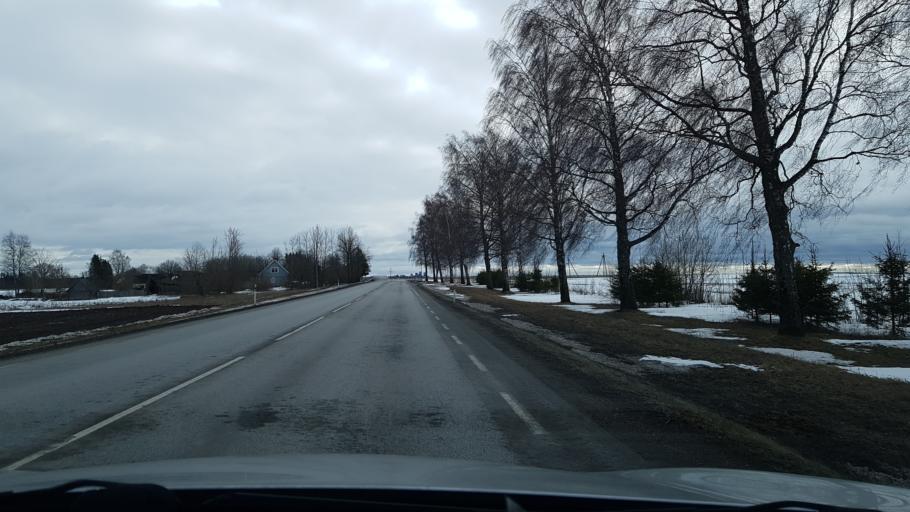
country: EE
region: Jogevamaa
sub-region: Jogeva linn
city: Jogeva
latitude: 58.7331
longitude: 26.3782
